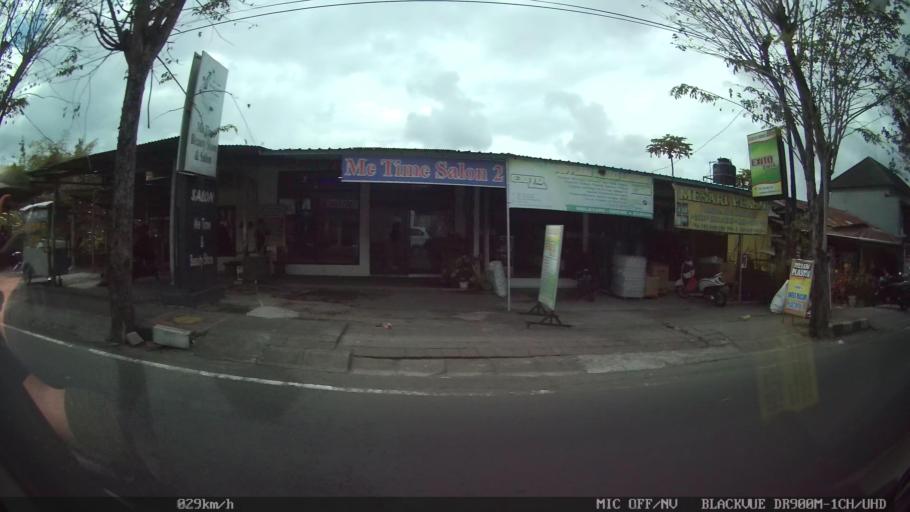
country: ID
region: Bali
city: Banjar Karangsuling
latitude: -8.6038
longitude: 115.1716
